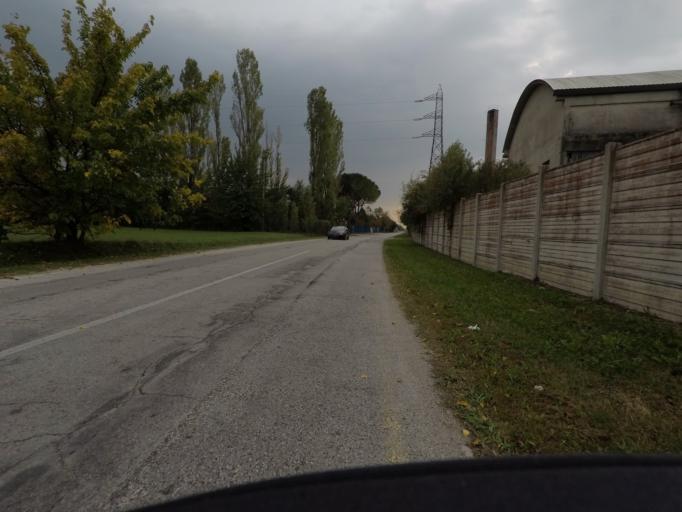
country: IT
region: Friuli Venezia Giulia
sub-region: Provincia di Udine
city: Feletto Umberto
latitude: 46.0972
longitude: 13.2419
